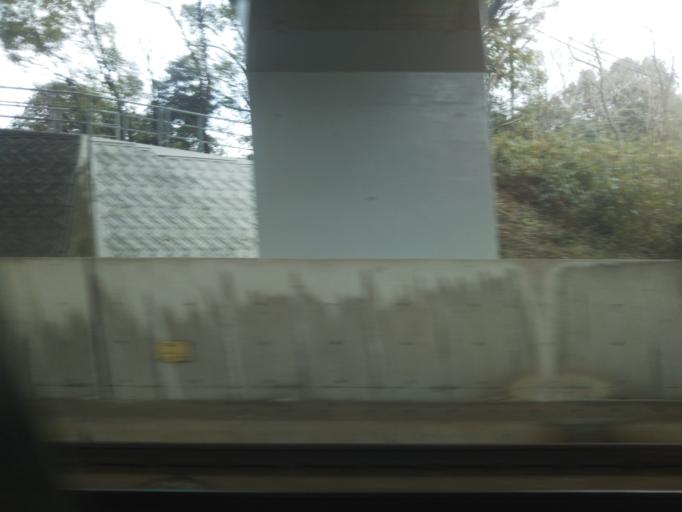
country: JP
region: Kagawa
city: Sakaidecho
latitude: 34.4226
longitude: 133.8039
